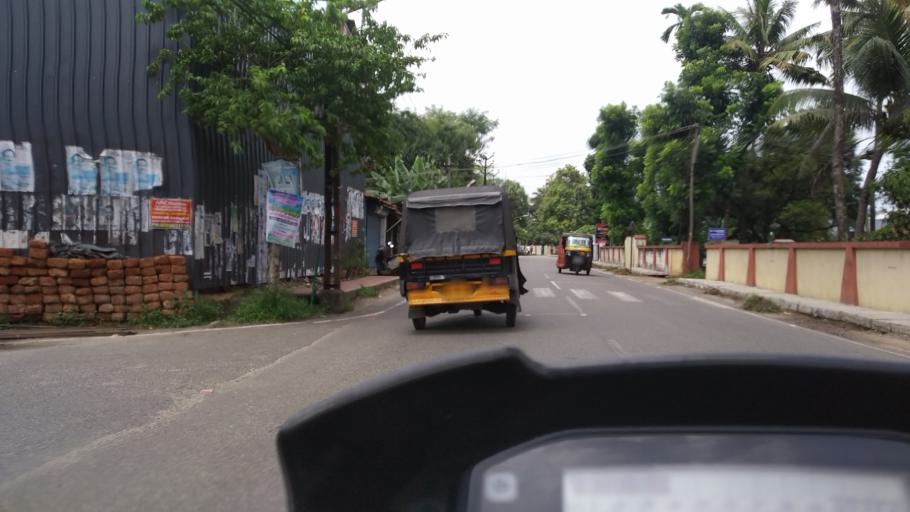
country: IN
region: Kerala
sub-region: Ernakulam
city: Aluva
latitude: 10.1204
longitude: 76.3393
